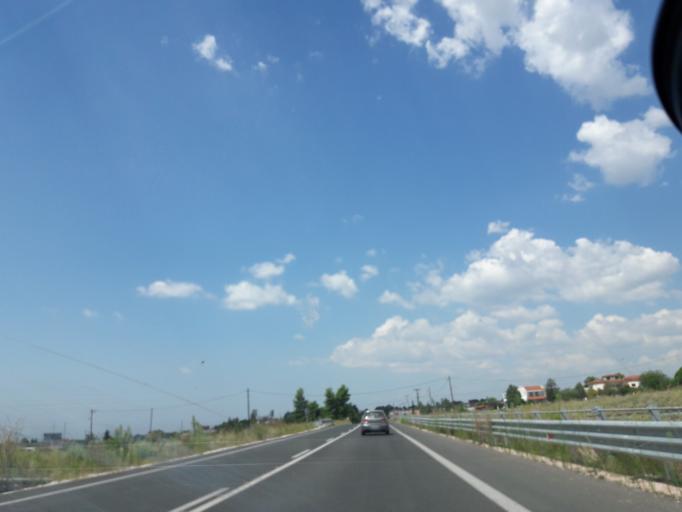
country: GR
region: Central Macedonia
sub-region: Nomos Thessalonikis
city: Agia Paraskevi
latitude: 40.5195
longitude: 23.0611
